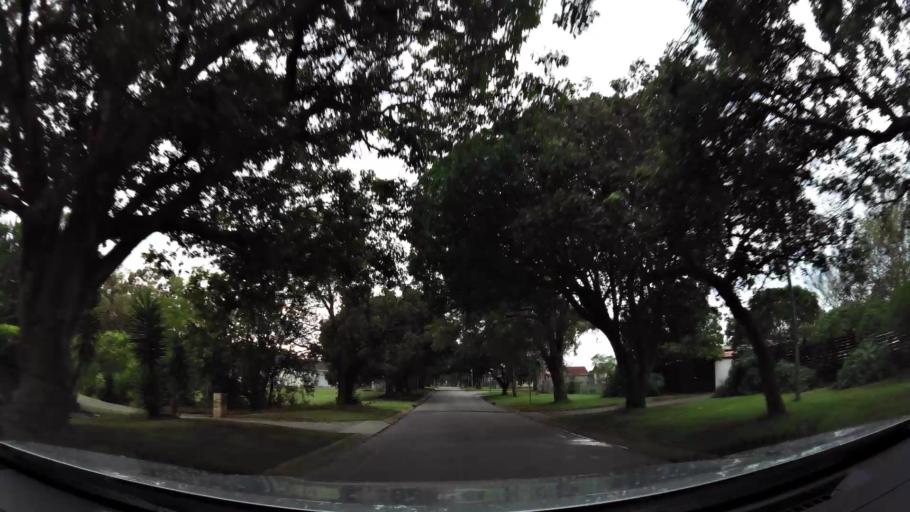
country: ZA
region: Eastern Cape
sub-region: Nelson Mandela Bay Metropolitan Municipality
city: Port Elizabeth
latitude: -33.9774
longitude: 25.5836
